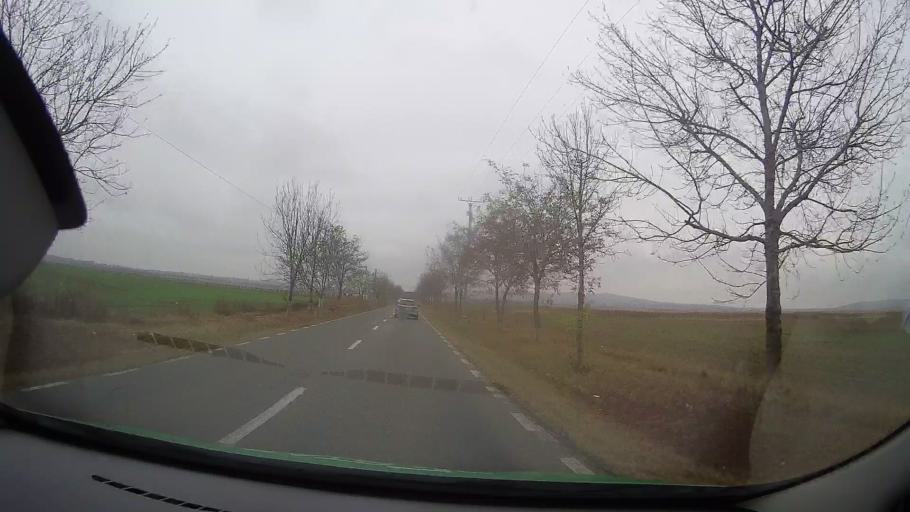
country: RO
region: Prahova
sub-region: Oras Baicoi
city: Liliesti
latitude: 45.0080
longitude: 25.8841
